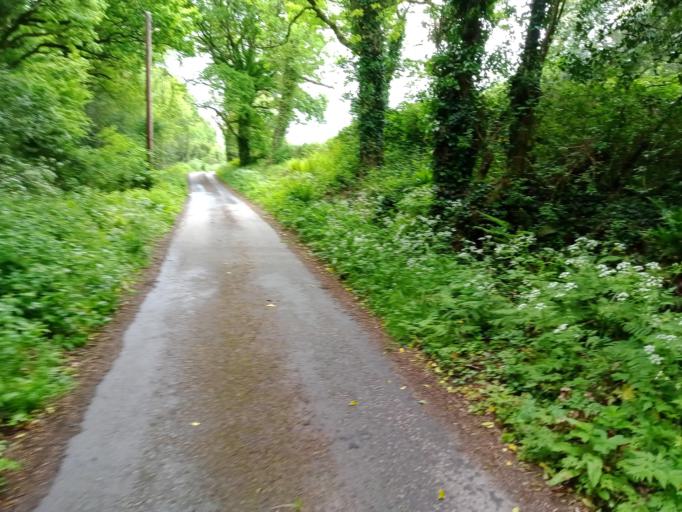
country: IE
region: Leinster
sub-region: Kilkenny
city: Thomastown
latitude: 52.5118
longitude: -7.1320
